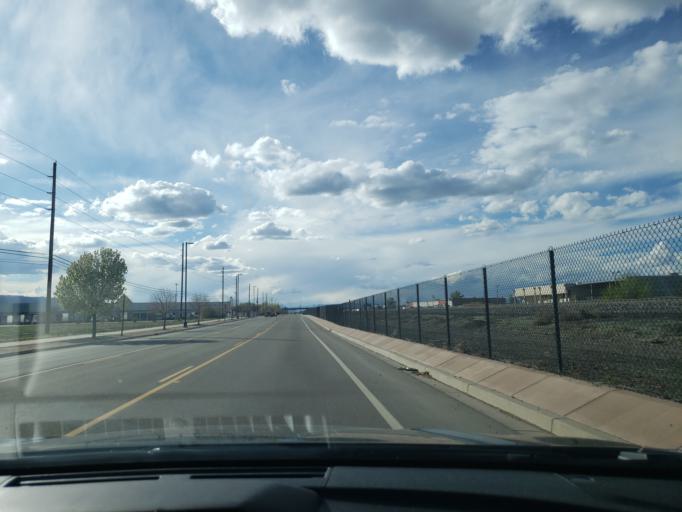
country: US
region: Colorado
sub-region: Mesa County
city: Redlands
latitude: 39.0859
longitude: -108.5992
